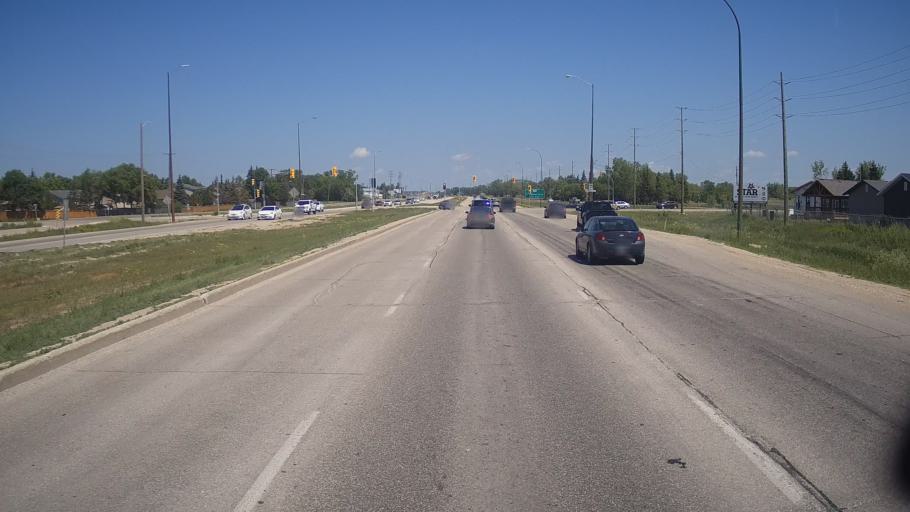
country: CA
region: Manitoba
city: Winnipeg
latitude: 49.9300
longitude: -97.0455
